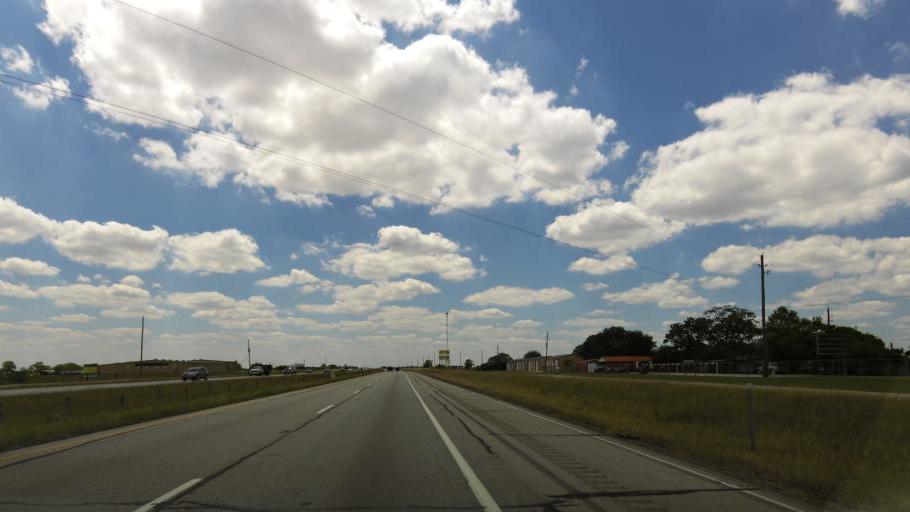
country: US
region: Texas
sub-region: Austin County
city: Sealy
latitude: 29.7514
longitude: -96.2806
